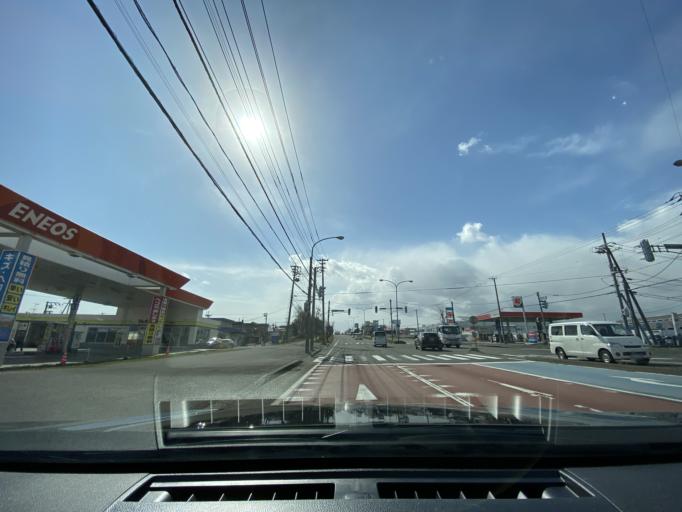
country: JP
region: Hokkaido
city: Kitahiroshima
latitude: 42.9658
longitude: 141.4856
